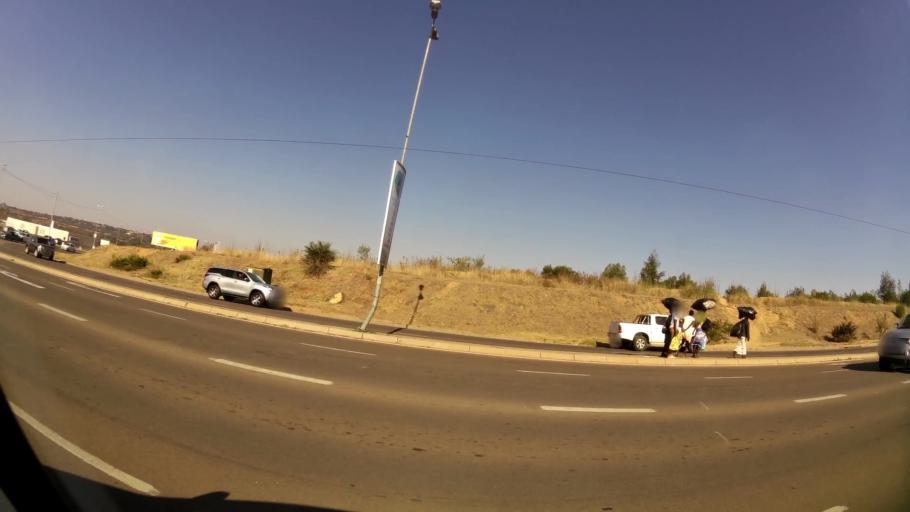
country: ZA
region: Gauteng
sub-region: City of Tshwane Metropolitan Municipality
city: Centurion
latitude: -25.8238
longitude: 28.3092
